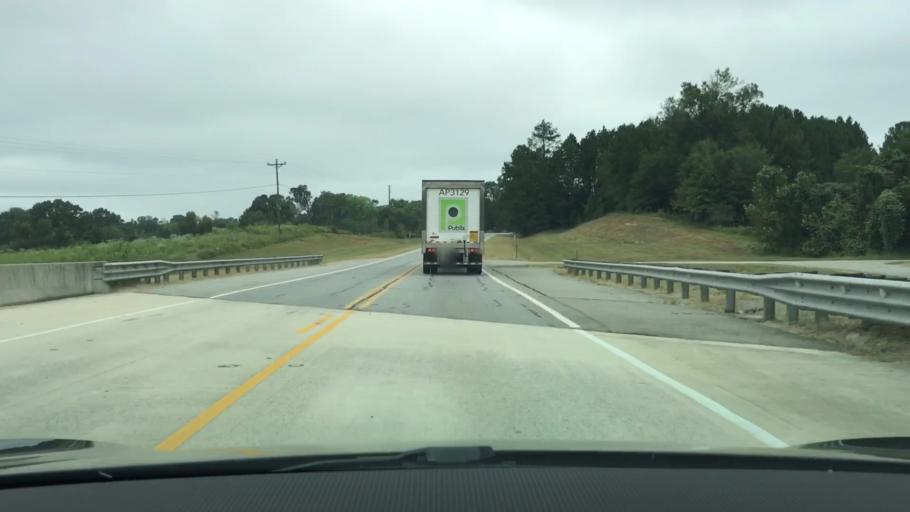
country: US
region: Georgia
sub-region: Oconee County
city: Watkinsville
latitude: 33.7368
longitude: -83.3035
